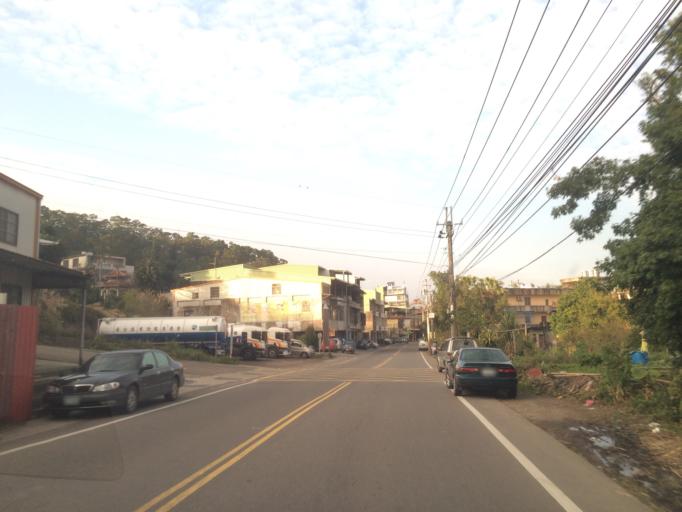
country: TW
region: Taiwan
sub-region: Hsinchu
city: Zhubei
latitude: 24.7085
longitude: 121.0970
